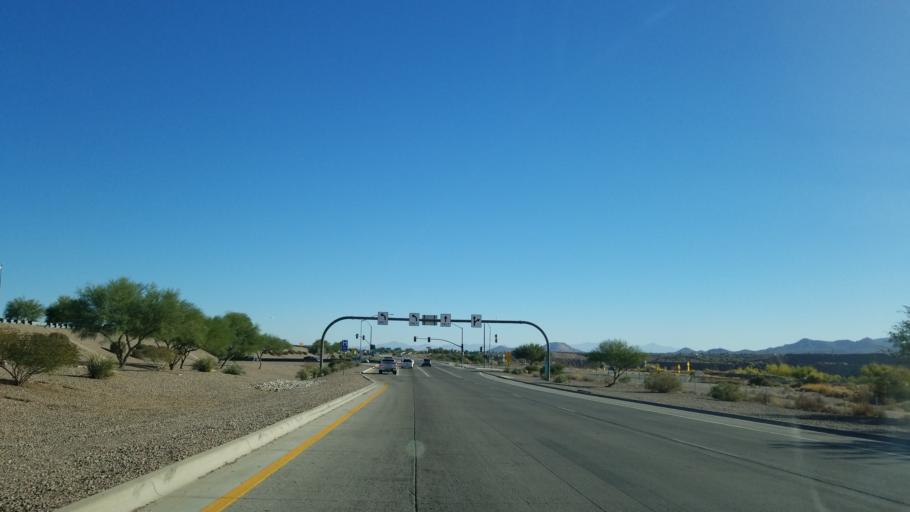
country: US
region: Arizona
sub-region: Pima County
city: Flowing Wells
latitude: 32.3244
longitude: -111.0534
